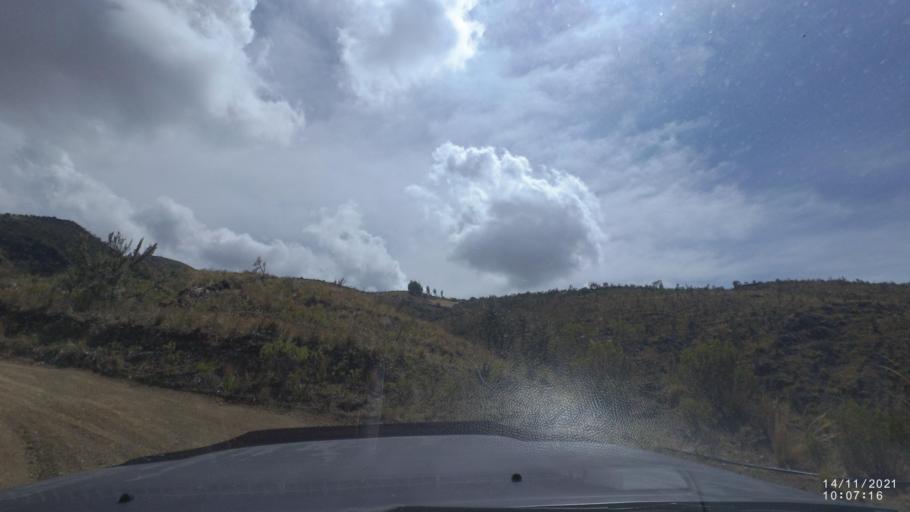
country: BO
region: Cochabamba
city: Cochabamba
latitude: -17.3483
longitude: -66.0891
